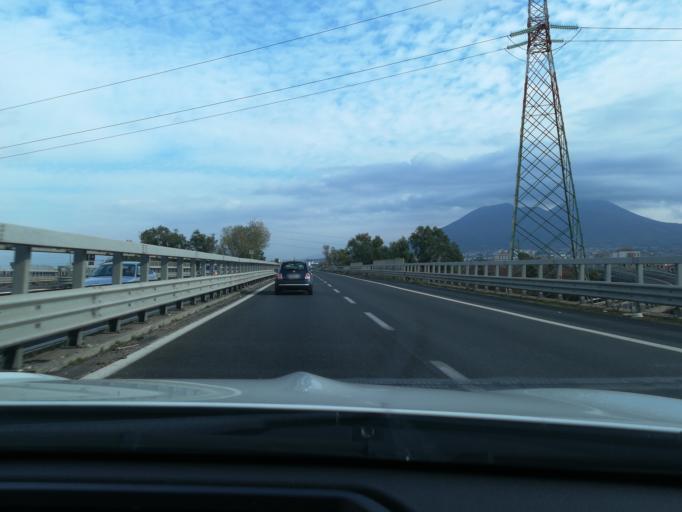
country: IT
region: Campania
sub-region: Provincia di Napoli
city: Arpino
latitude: 40.8667
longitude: 14.3188
